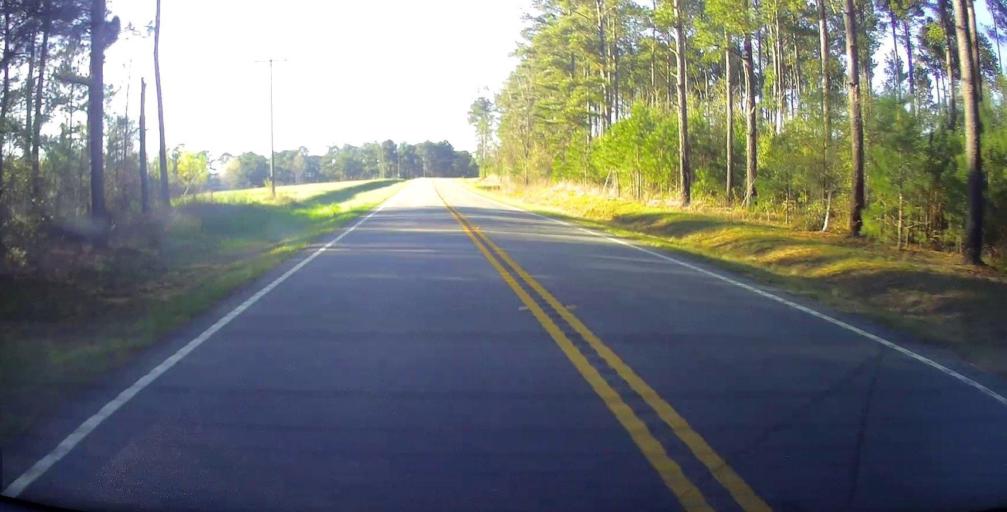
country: US
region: Georgia
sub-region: Pulaski County
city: Hawkinsville
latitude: 32.2101
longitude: -83.3801
